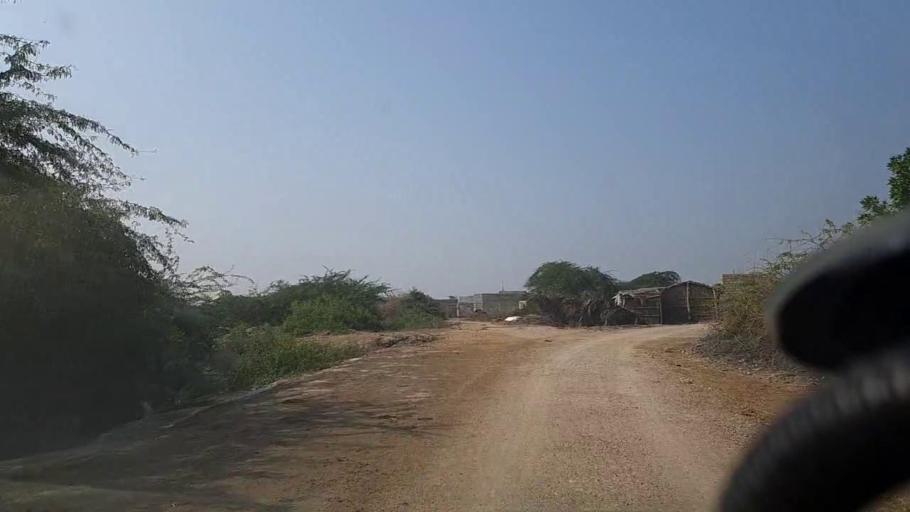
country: PK
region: Sindh
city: Thatta
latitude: 24.6648
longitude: 67.9231
